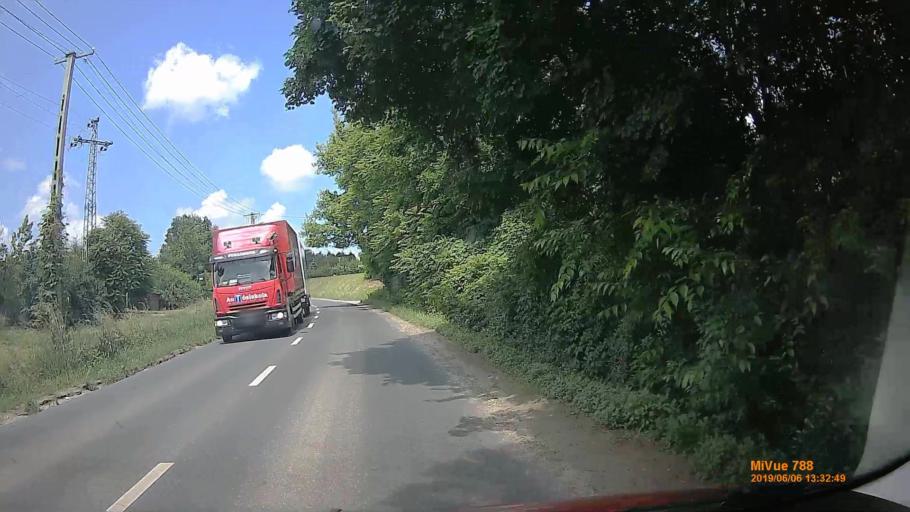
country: HU
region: Pest
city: Vac
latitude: 47.7876
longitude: 19.1464
